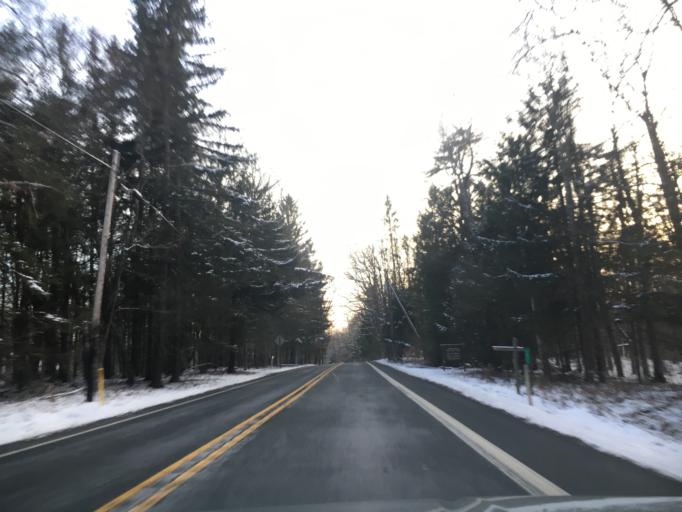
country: US
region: Pennsylvania
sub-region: Pike County
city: Saw Creek
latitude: 41.2151
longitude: -75.0815
